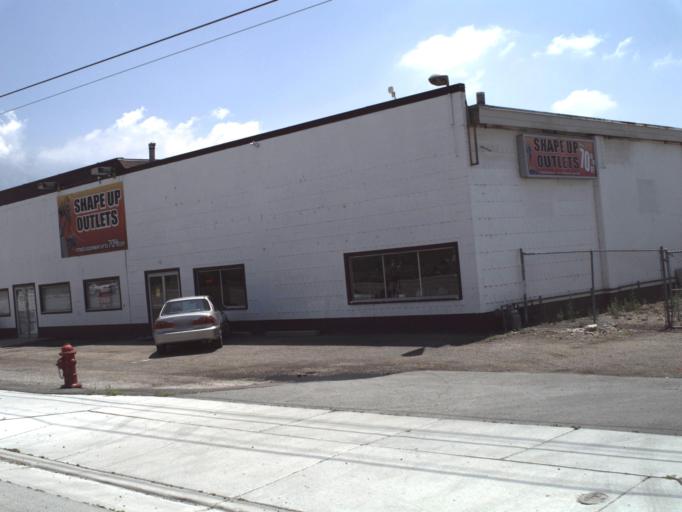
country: US
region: Utah
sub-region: Weber County
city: Marriott-Slaterville
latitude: 41.2445
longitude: -112.0002
